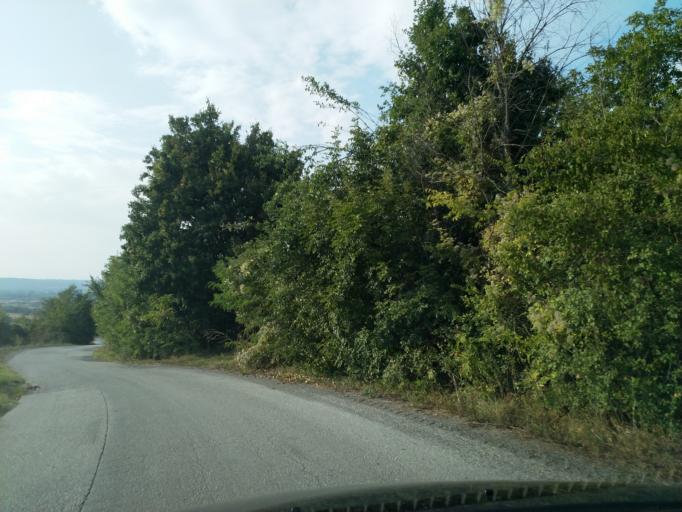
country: RS
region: Central Serbia
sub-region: Pomoravski Okrug
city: Paracin
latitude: 43.8438
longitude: 21.5291
